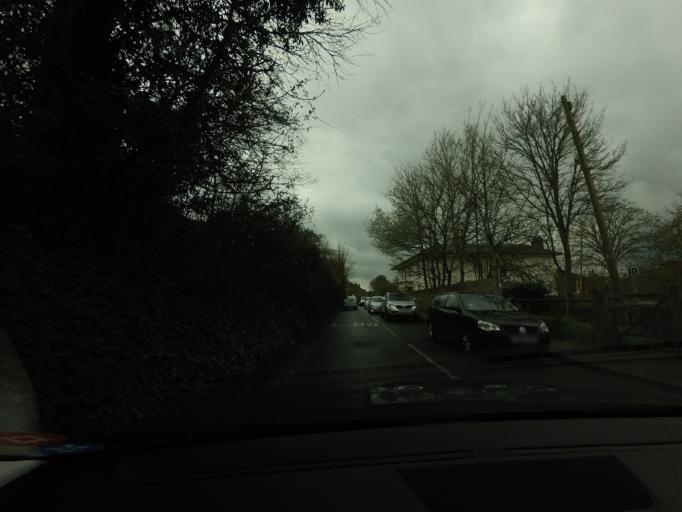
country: GB
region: England
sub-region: Kent
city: Eynsford
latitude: 51.3728
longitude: 0.2191
